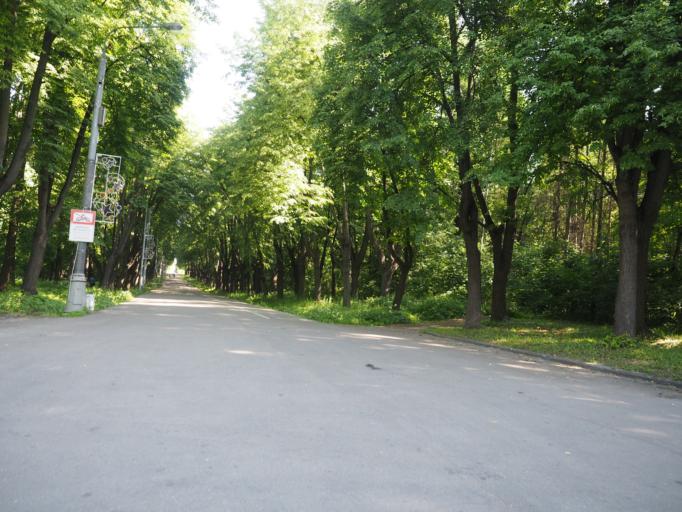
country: RU
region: Moscow
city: Ryazanskiy
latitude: 55.7767
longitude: 37.7486
